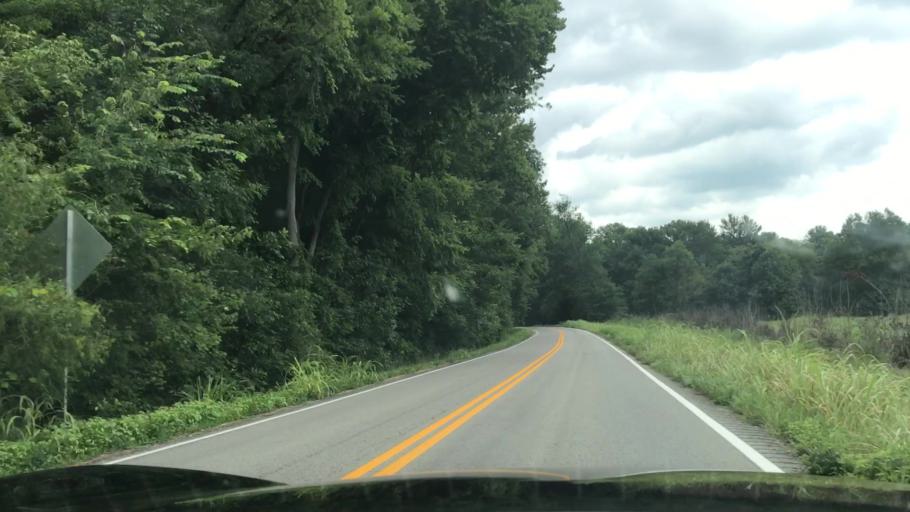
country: US
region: Kentucky
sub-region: Muhlenberg County
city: Central City
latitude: 37.1975
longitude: -87.0346
